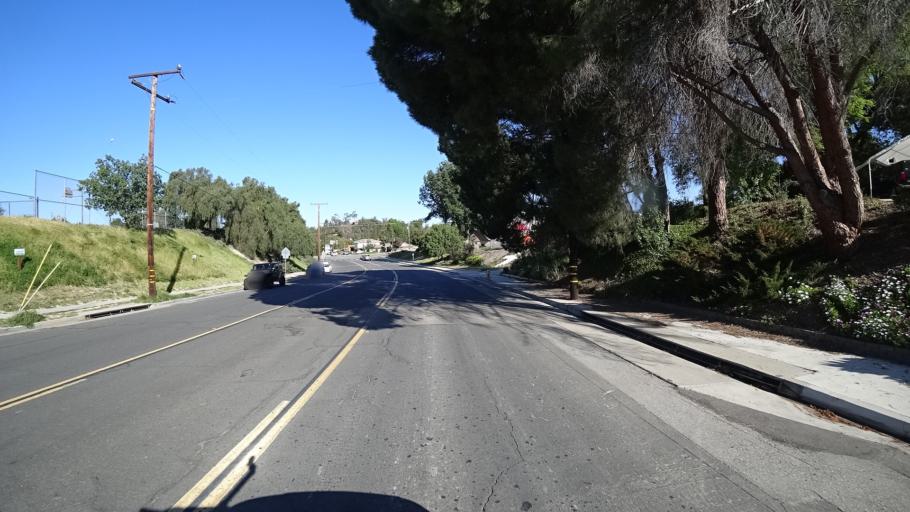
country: US
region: California
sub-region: Ventura County
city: Thousand Oaks
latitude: 34.1937
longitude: -118.8416
